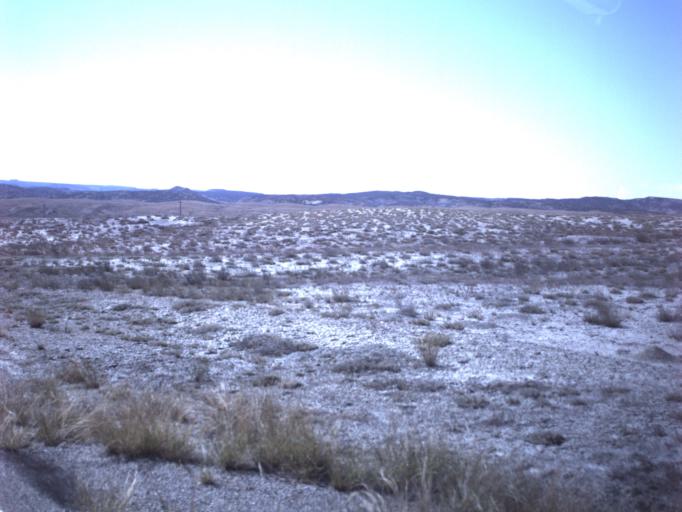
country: US
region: Utah
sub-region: Grand County
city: Moab
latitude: 38.8923
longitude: -109.3111
